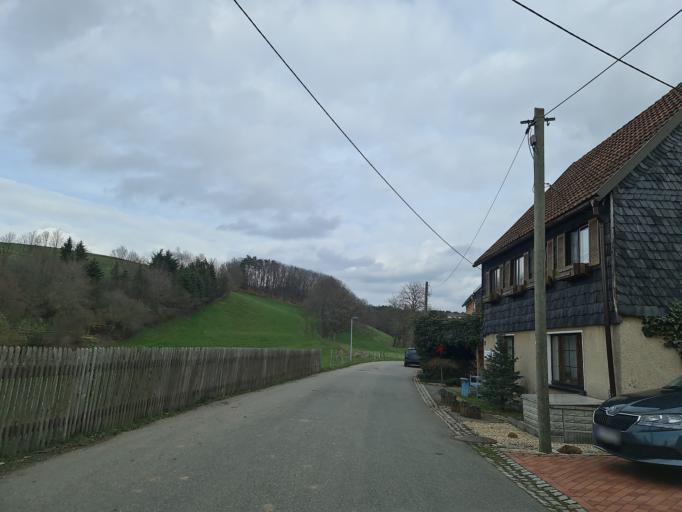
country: DE
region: Saxony
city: Reinsdorf
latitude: 50.7030
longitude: 12.6173
